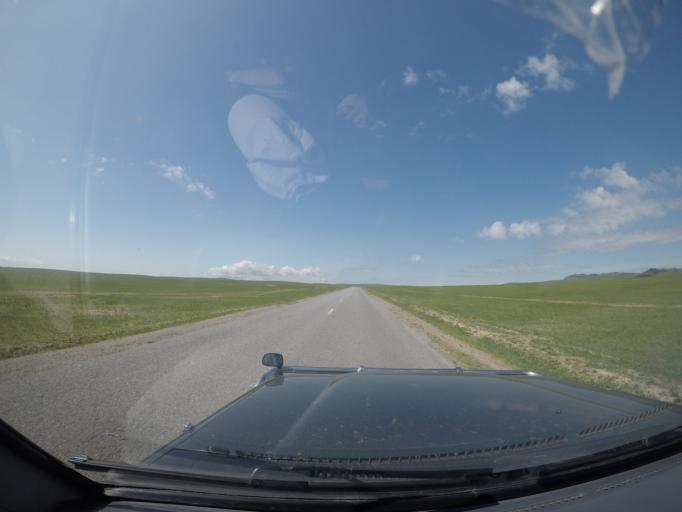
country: MN
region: Hentiy
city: Bayan
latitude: 47.3193
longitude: 111.3981
